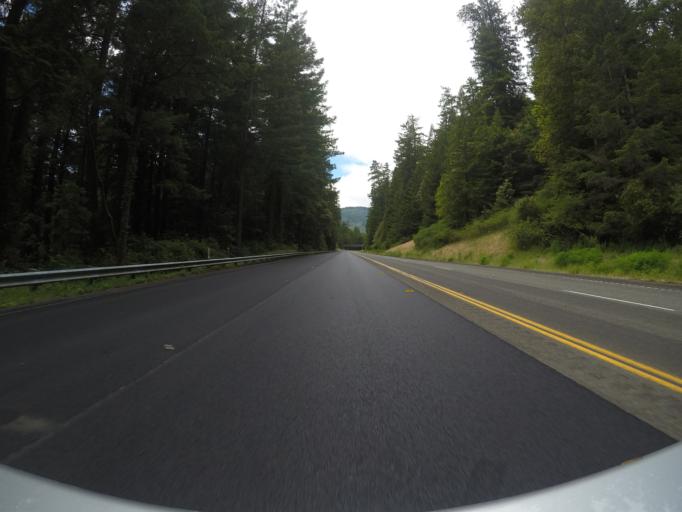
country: US
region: California
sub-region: Humboldt County
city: Redway
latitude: 40.3049
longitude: -123.8968
